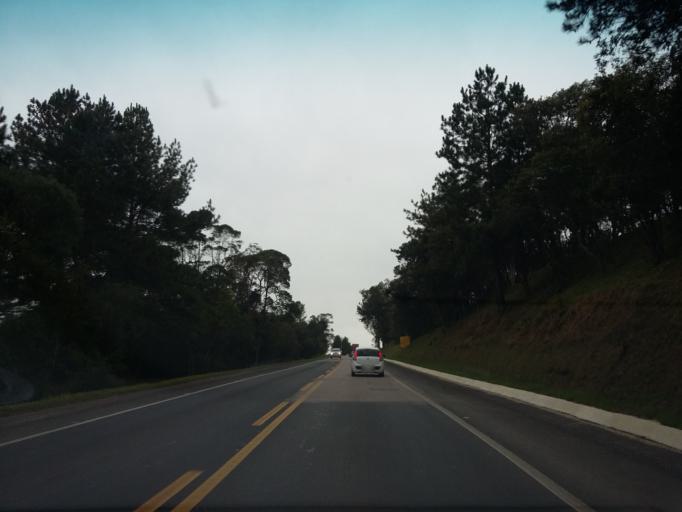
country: BR
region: Santa Catarina
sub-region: Santa Cecilia
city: Santa Cecilia
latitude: -26.6767
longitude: -50.2890
